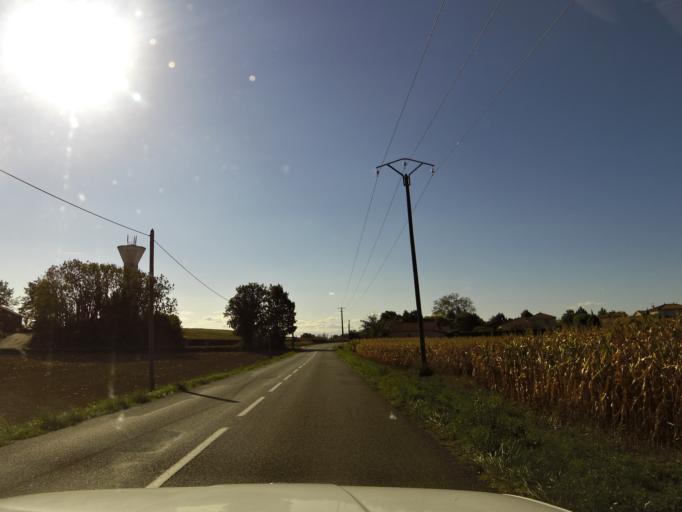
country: FR
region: Rhone-Alpes
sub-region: Departement de l'Ain
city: Chazey-sur-Ain
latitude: 45.8860
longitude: 5.2857
